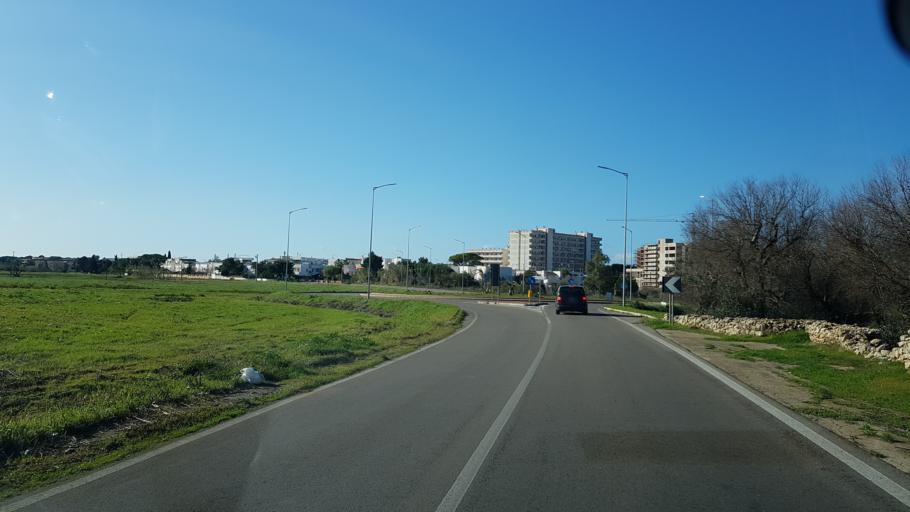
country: IT
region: Apulia
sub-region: Provincia di Lecce
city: Gallipoli
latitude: 40.0915
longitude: 18.0183
